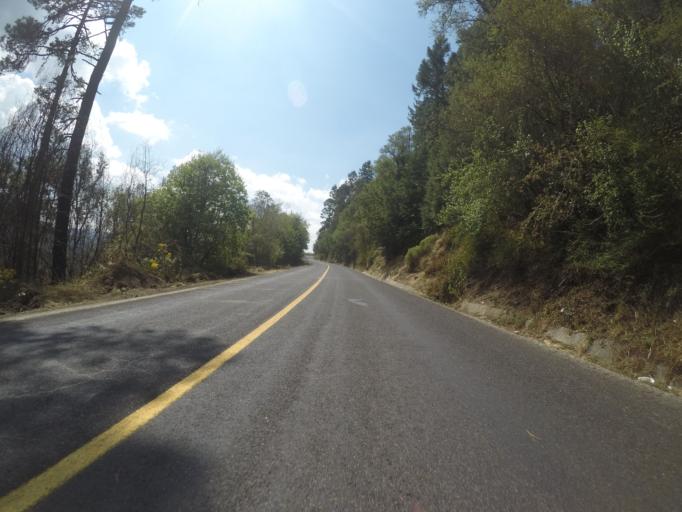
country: MX
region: Mexico
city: Cerro La Calera
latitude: 19.1457
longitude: -99.8067
